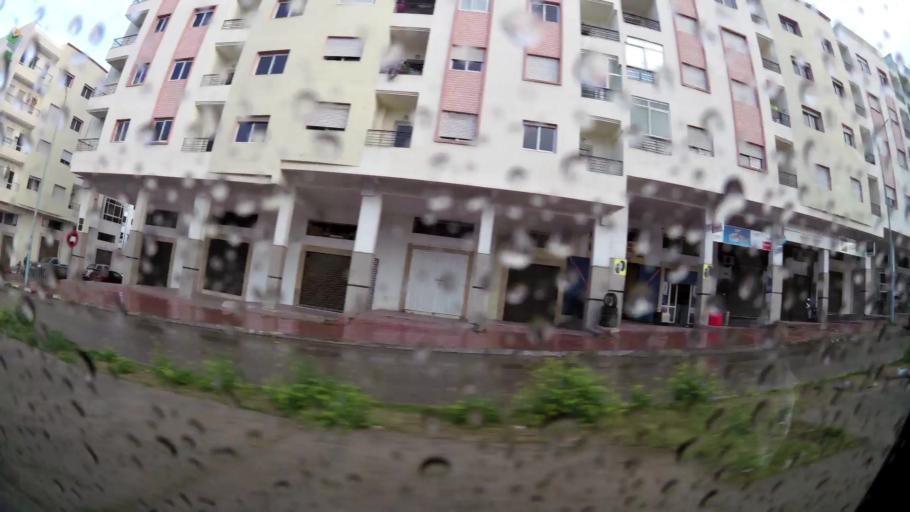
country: MA
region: Doukkala-Abda
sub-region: El-Jadida
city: El Jadida
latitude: 33.2262
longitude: -8.4945
